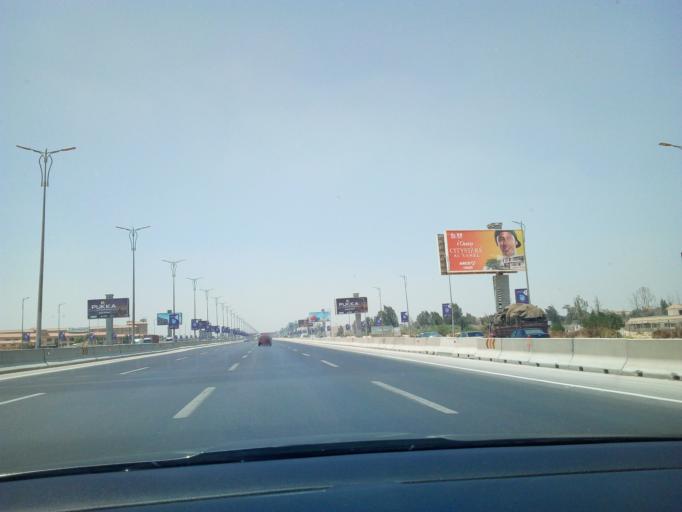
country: EG
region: Al Jizah
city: Awsim
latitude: 30.0547
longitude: 31.0399
